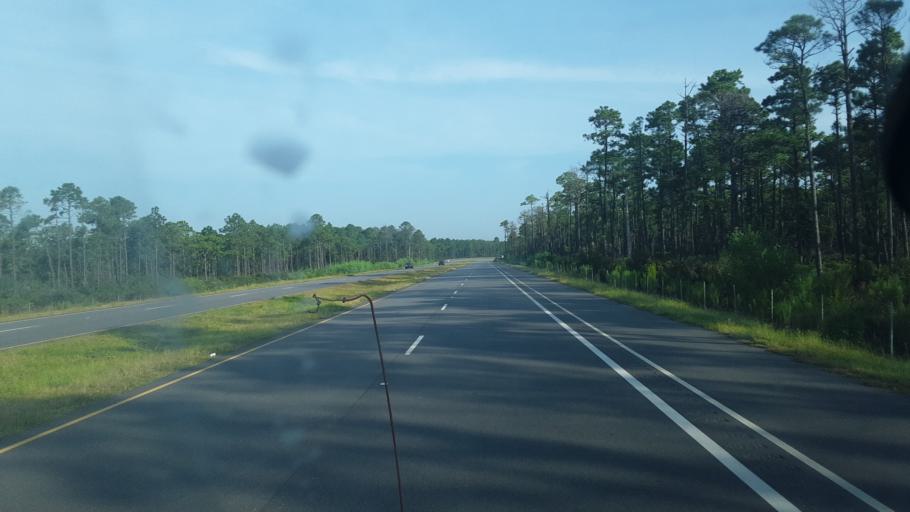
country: US
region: South Carolina
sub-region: Horry County
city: Myrtle Beach
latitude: 33.7891
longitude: -78.8797
